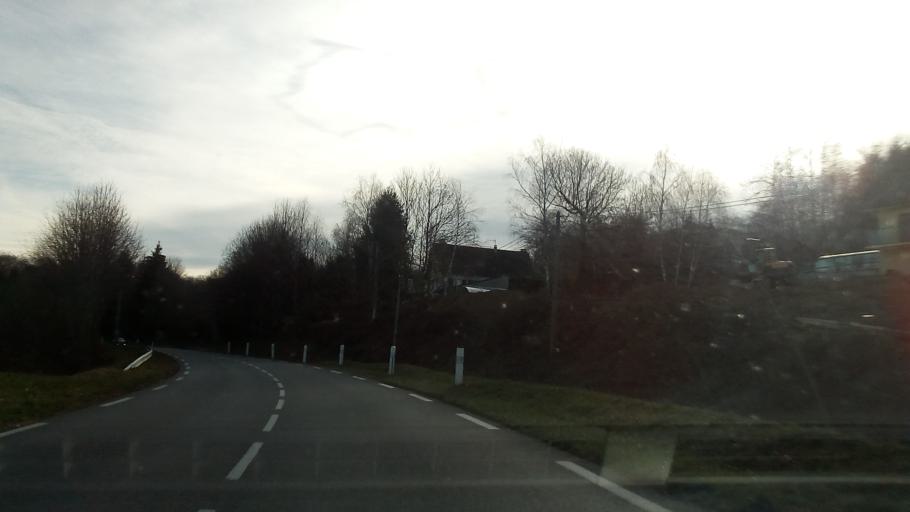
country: FR
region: Limousin
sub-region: Departement de la Correze
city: Naves
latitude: 45.3348
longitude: 1.7523
